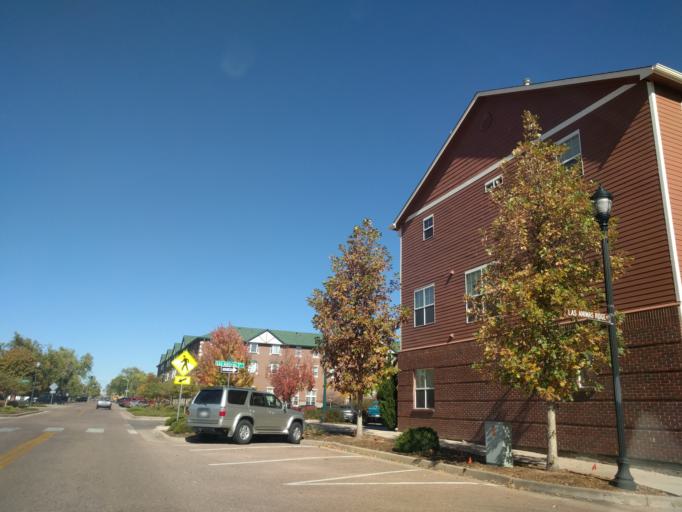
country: US
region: Colorado
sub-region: El Paso County
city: Colorado Springs
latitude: 38.8225
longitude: -104.8204
